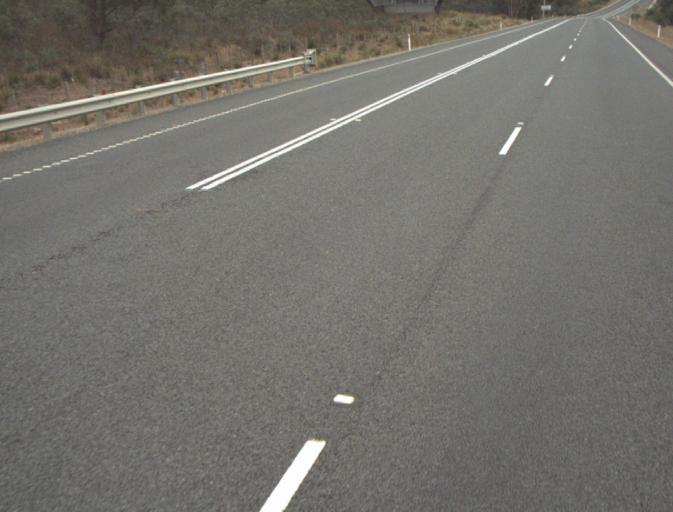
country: AU
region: Tasmania
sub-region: Launceston
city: Mayfield
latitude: -41.2641
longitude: 147.0312
